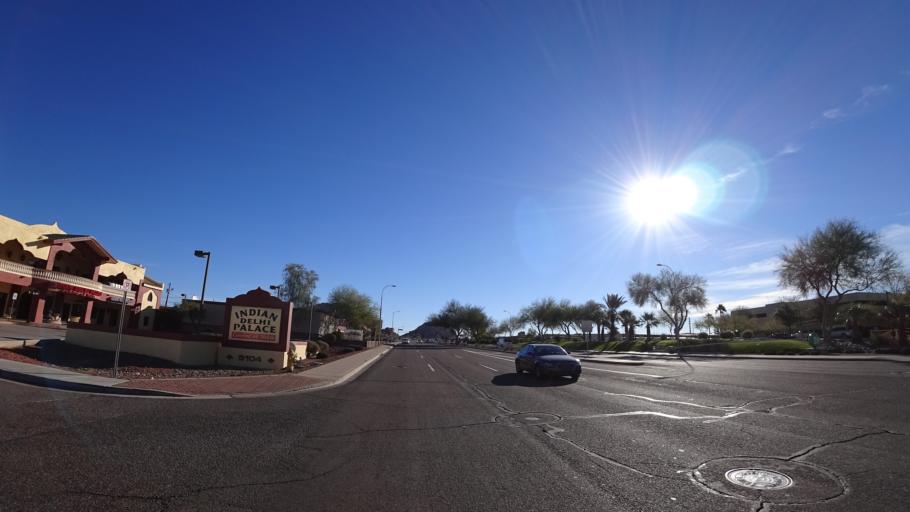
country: US
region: Arizona
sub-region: Maricopa County
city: Tempe Junction
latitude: 33.4657
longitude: -111.9721
